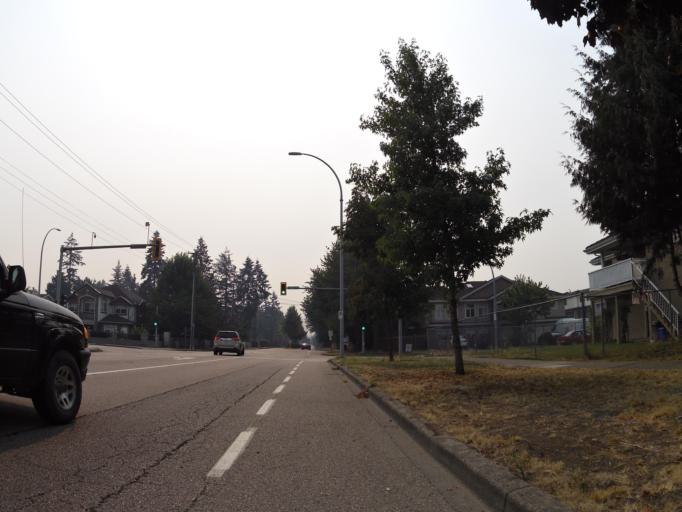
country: CA
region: British Columbia
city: Surrey
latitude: 49.1315
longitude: -122.8568
